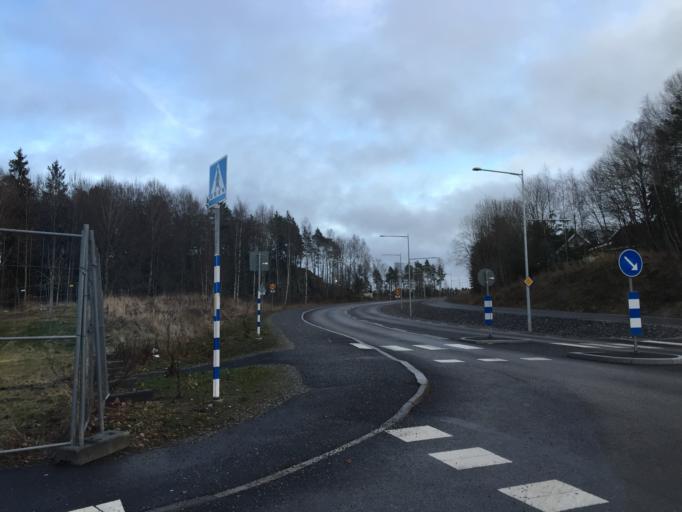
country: SE
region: Stockholm
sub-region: Sodertalje Kommun
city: Soedertaelje
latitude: 59.2215
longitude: 17.6414
